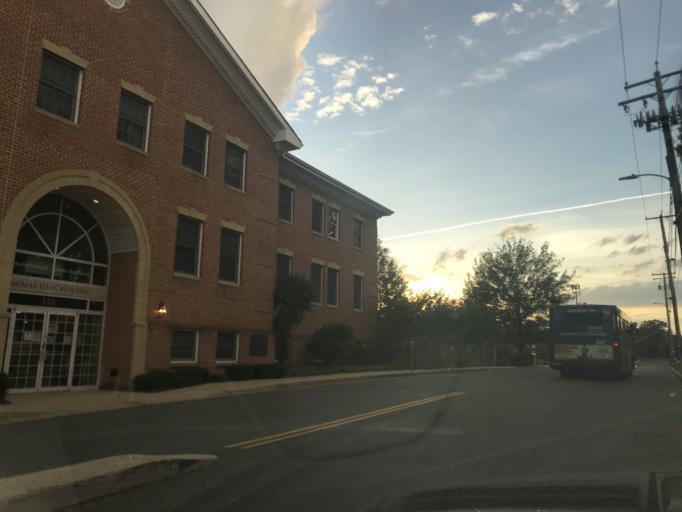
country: US
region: Maryland
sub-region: Harford County
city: Bel Air
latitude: 39.5332
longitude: -76.3500
